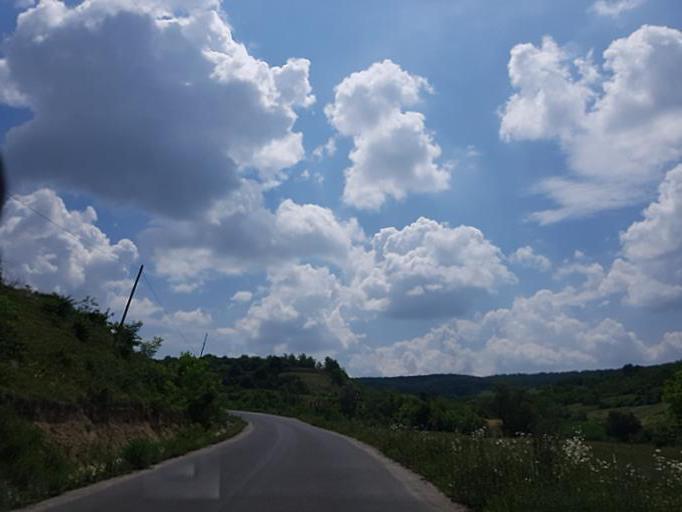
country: RO
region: Sibiu
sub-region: Comuna Seica Mica
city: Seica Mica
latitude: 46.0495
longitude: 24.1463
